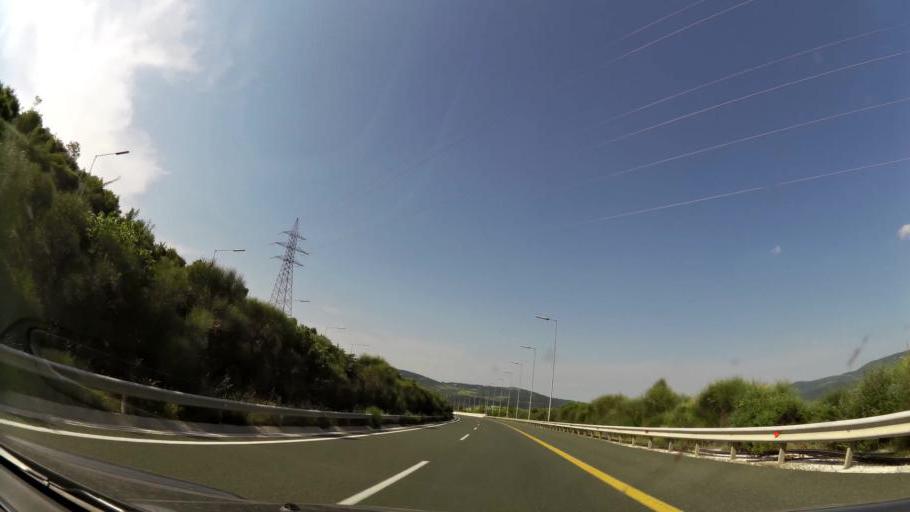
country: GR
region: Central Macedonia
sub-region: Nomos Imathias
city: Rizomata
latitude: 40.4137
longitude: 22.1797
